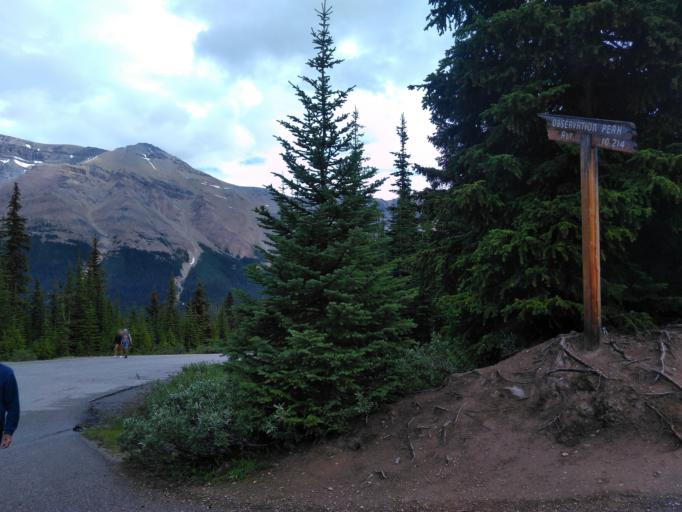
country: CA
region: Alberta
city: Lake Louise
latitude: 51.7167
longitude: -116.5062
